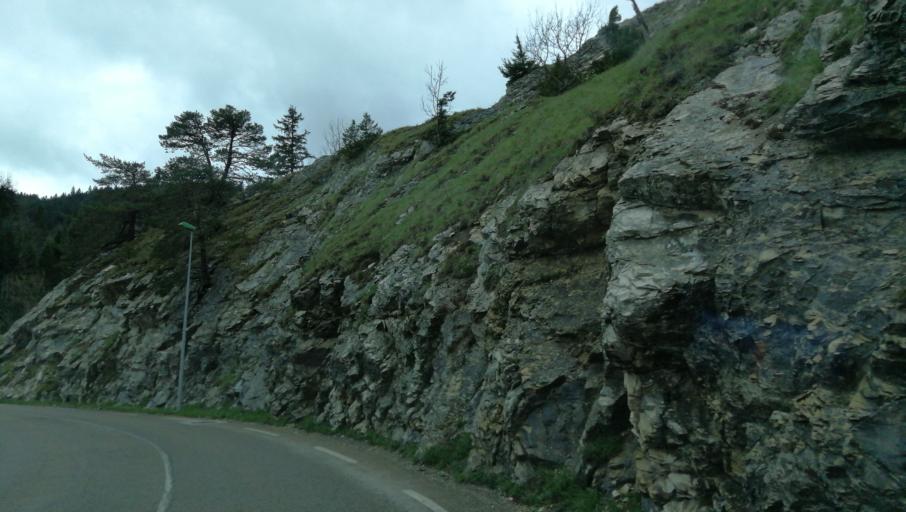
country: FR
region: Rhone-Alpes
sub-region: Departement de l'Isere
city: Villard-de-Lans
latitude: 45.0738
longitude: 5.5410
